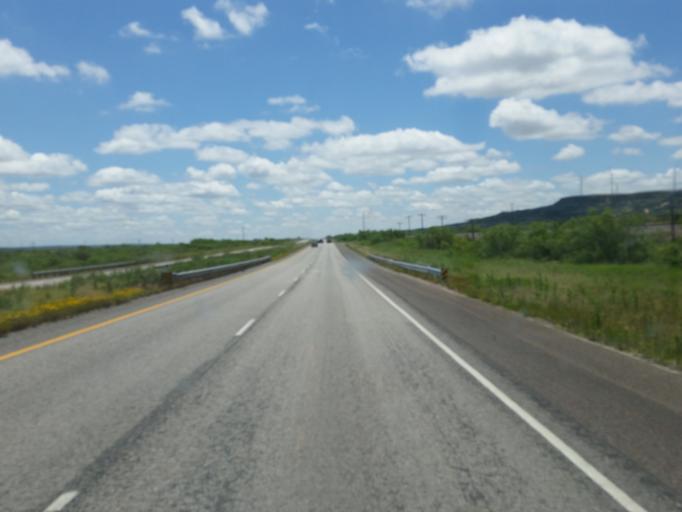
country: US
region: Texas
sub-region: Scurry County
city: Snyder
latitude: 32.9761
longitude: -101.1026
